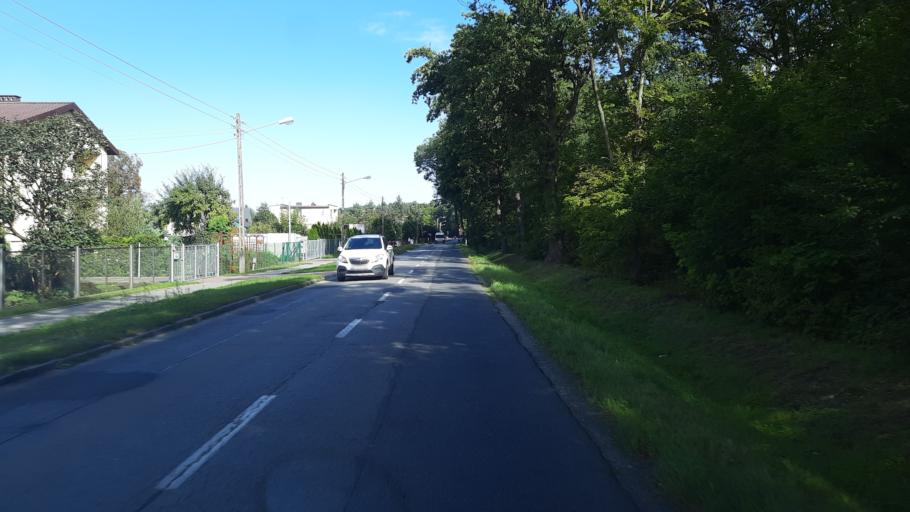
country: PL
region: Lower Silesian Voivodeship
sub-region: Powiat wroclawski
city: Dlugoleka
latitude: 51.1804
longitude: 17.1900
